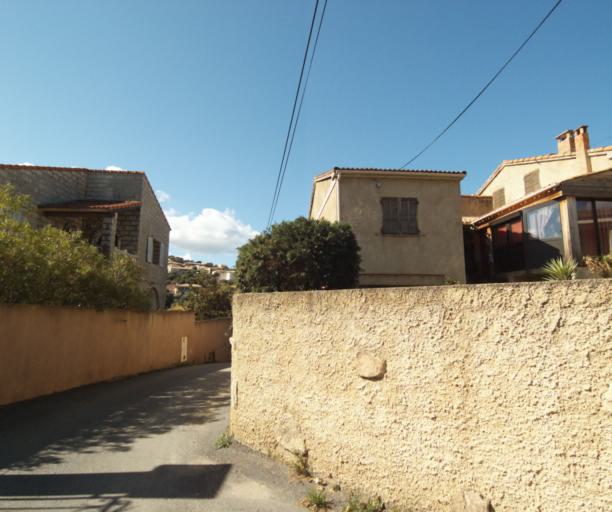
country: FR
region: Corsica
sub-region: Departement de la Corse-du-Sud
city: Propriano
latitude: 41.6740
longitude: 8.9037
